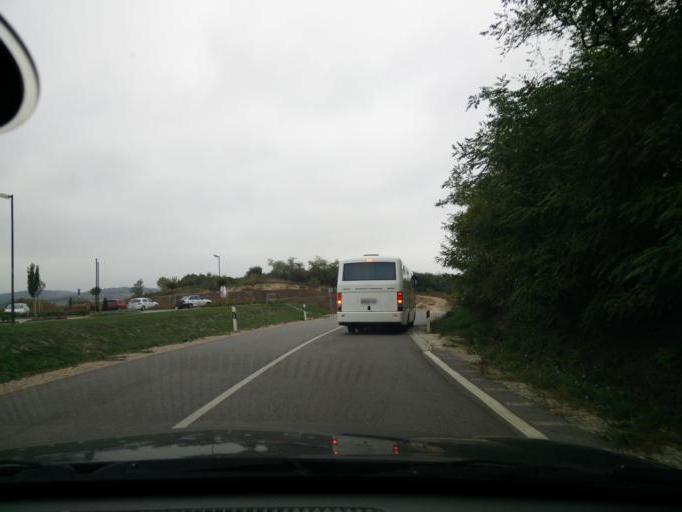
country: HU
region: Komarom-Esztergom
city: Bajna
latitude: 47.6855
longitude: 18.6090
